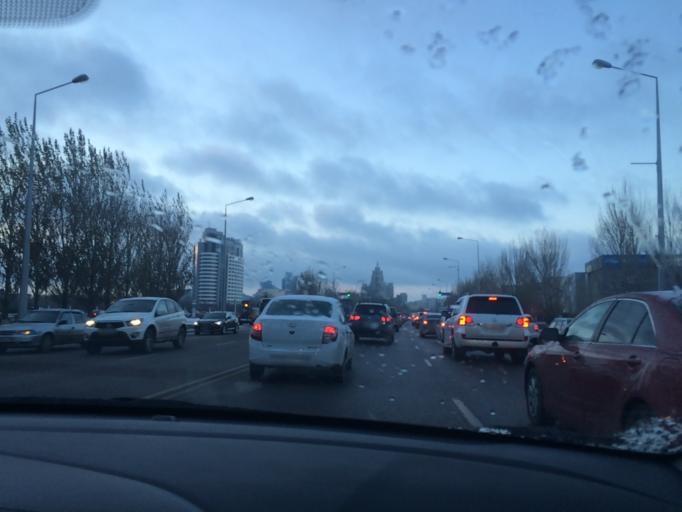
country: KZ
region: Astana Qalasy
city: Astana
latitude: 51.1537
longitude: 71.4125
